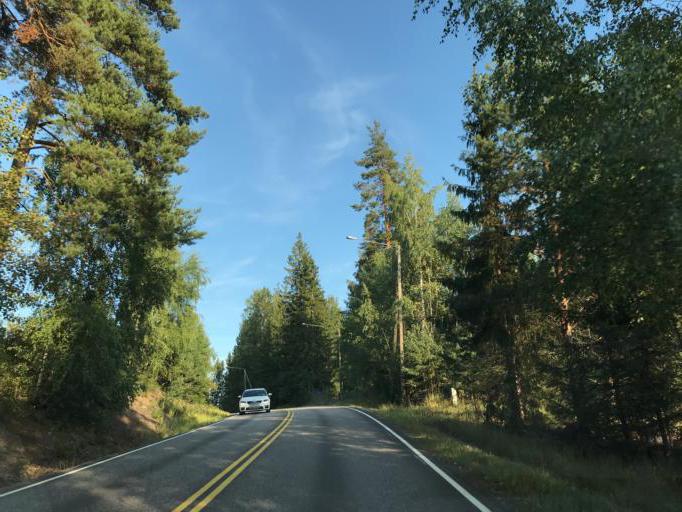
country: FI
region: Uusimaa
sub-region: Helsinki
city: Vihti
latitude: 60.4109
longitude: 24.4411
